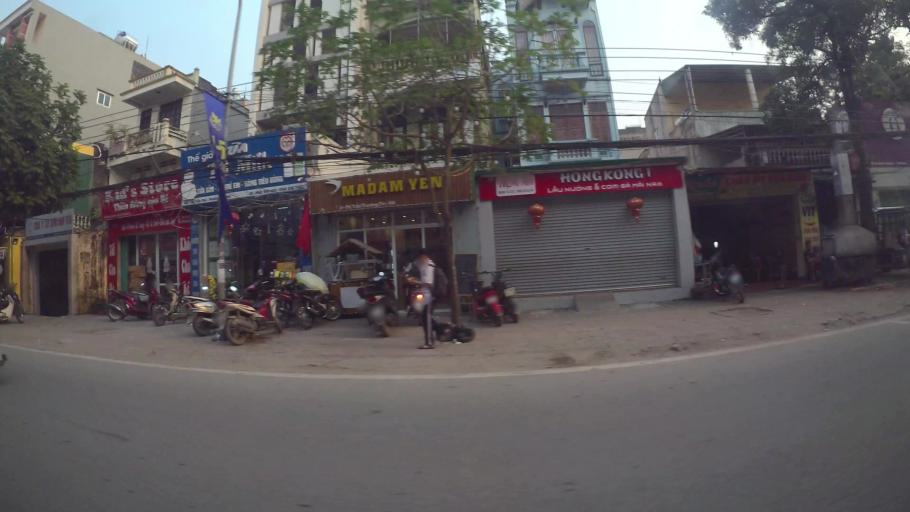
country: VN
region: Ha Noi
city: Thuong Tin
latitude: 20.8676
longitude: 105.8611
